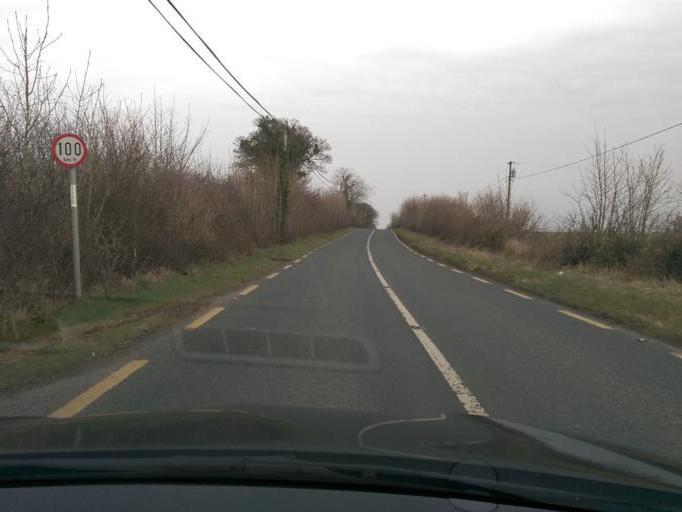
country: IE
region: Connaught
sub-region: Roscommon
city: Roscommon
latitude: 53.5123
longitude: -8.3587
